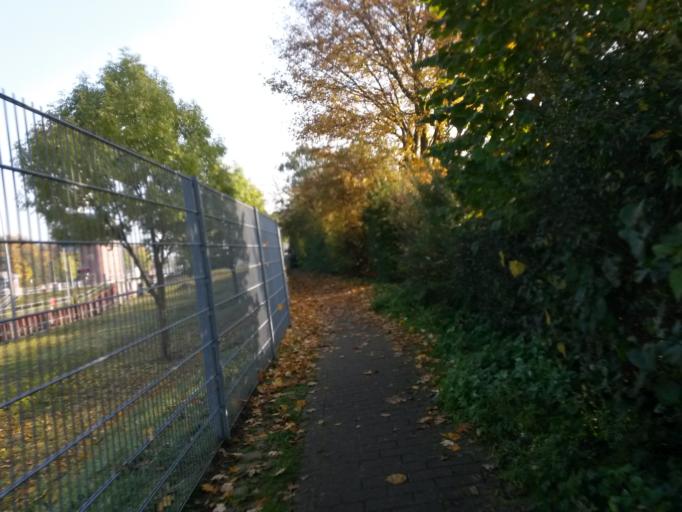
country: DE
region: Bremen
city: Bremen
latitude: 53.0589
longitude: 8.8593
